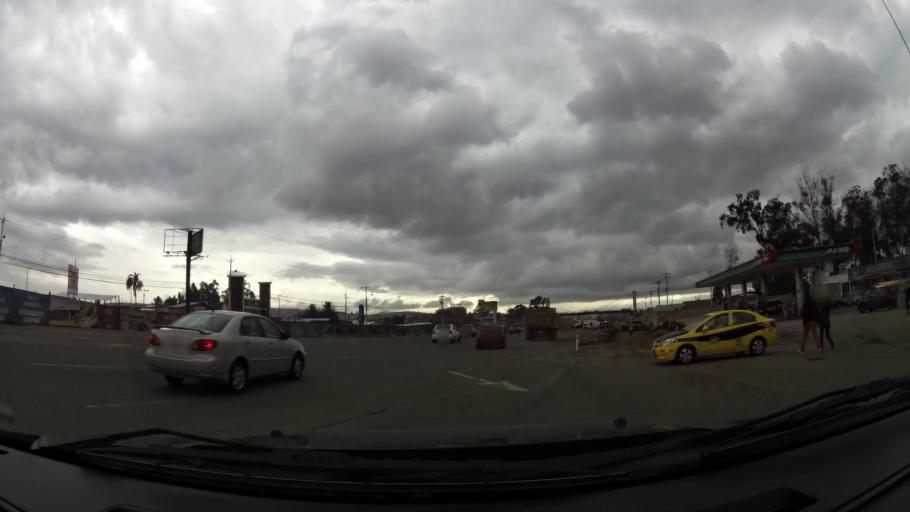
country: EC
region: Pichincha
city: Quito
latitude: -0.1094
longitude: -78.4576
